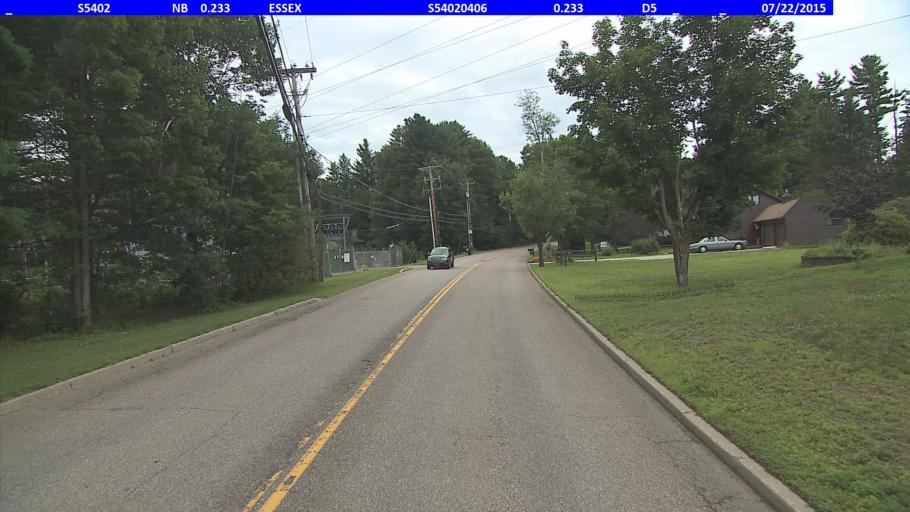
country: US
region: Vermont
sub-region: Chittenden County
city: Williston
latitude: 44.4822
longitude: -73.0502
